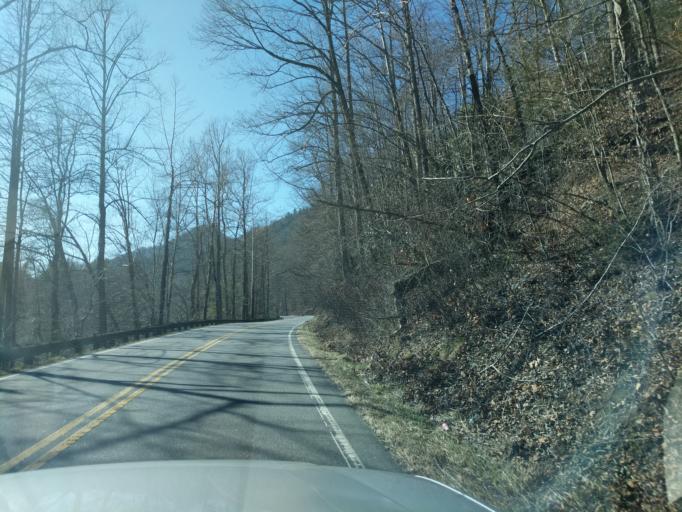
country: US
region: North Carolina
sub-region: Graham County
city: Robbinsville
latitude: 35.2810
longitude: -83.6761
